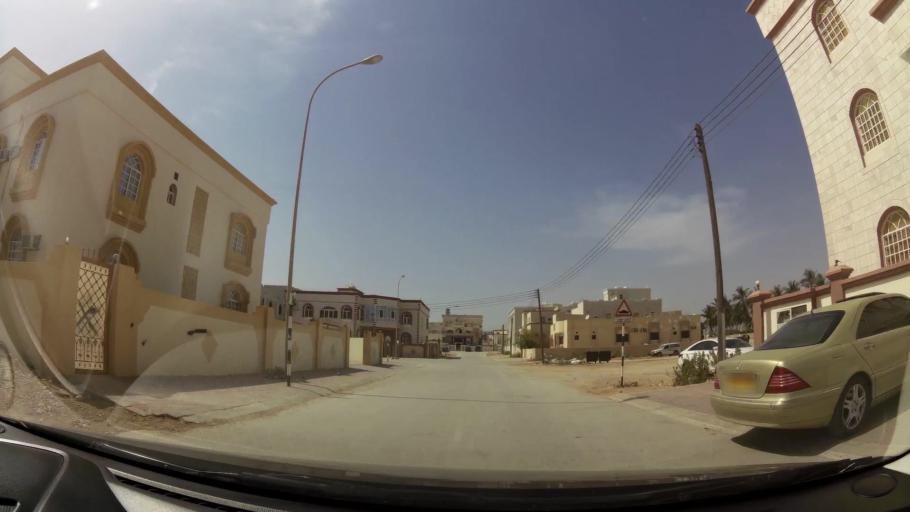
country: OM
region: Zufar
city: Salalah
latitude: 17.0483
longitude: 54.1604
